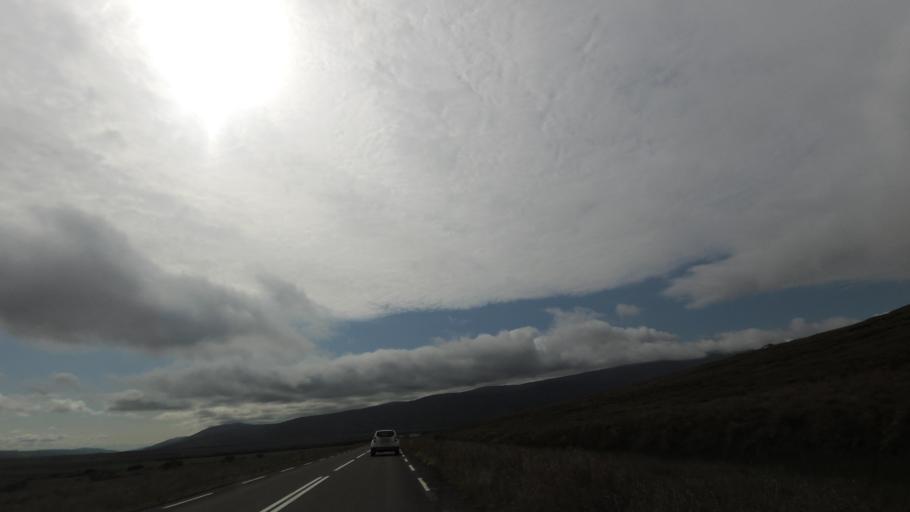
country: IS
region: Northeast
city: Laugar
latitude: 65.7221
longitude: -17.5981
